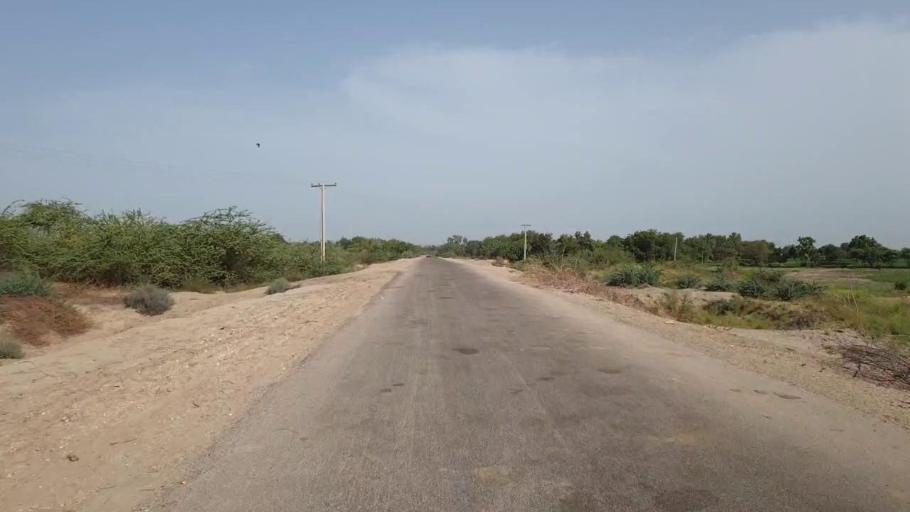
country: PK
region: Sindh
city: Sakrand
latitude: 26.2692
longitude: 68.2782
